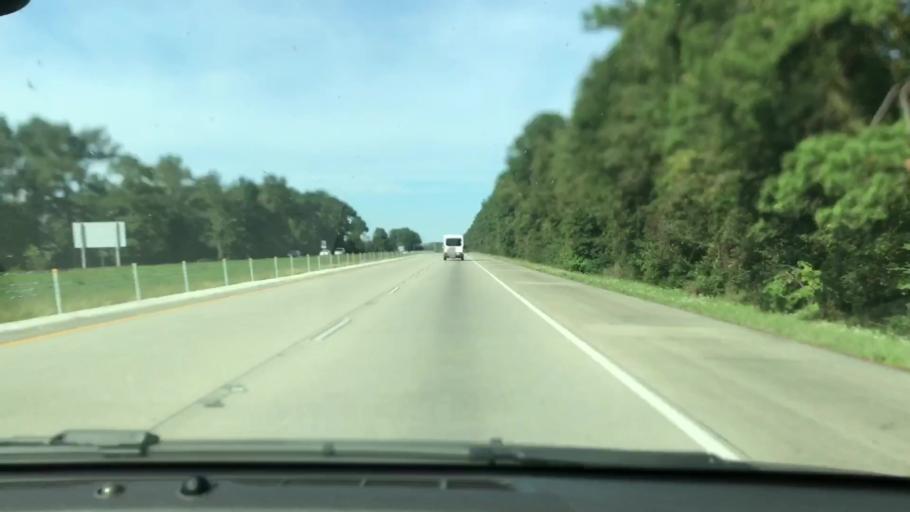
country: US
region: Louisiana
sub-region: Saint Tammany Parish
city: Pearl River
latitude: 30.3261
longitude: -89.7375
